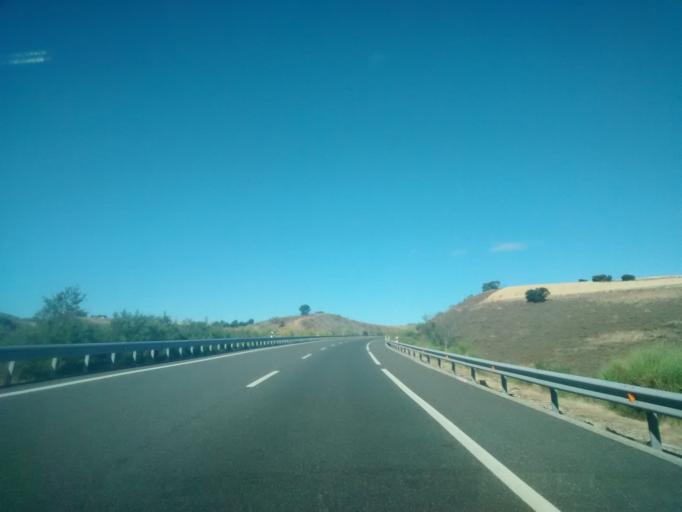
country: ES
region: Castille and Leon
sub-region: Provincia de Segovia
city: Villacastin
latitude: 40.7524
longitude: -4.4579
